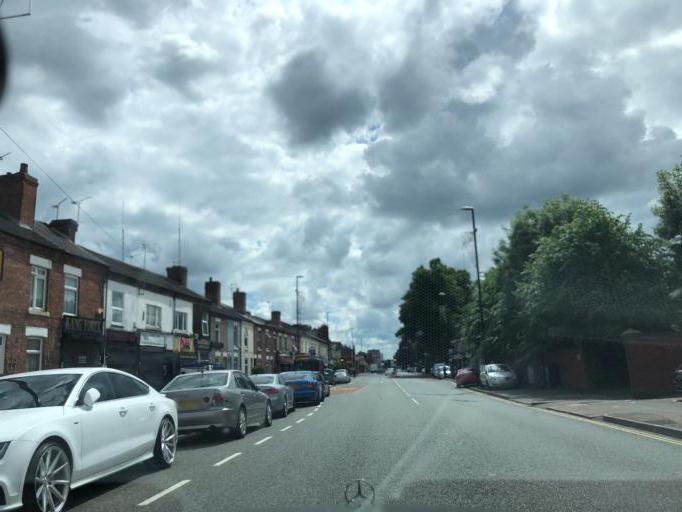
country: GB
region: England
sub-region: Coventry
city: Coventry
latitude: 52.4275
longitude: -1.5001
